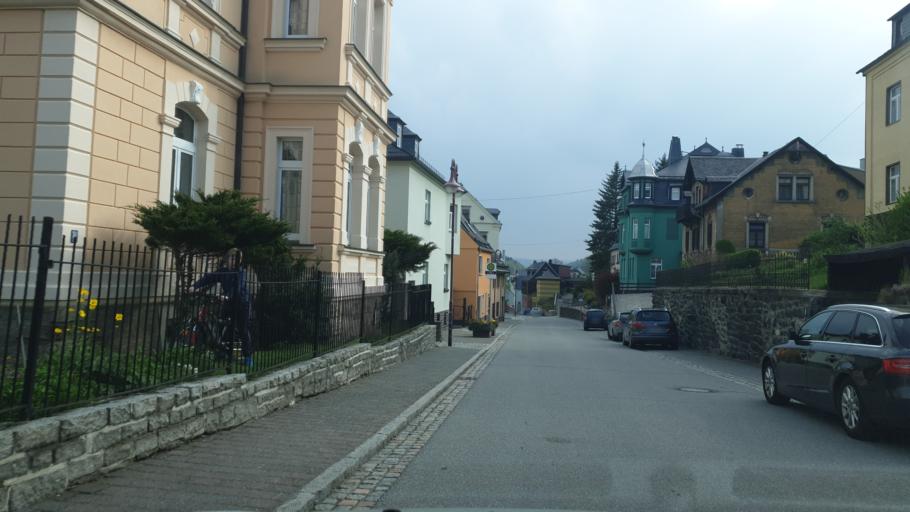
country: DE
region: Saxony
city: Lossnitz
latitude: 50.6195
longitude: 12.7290
